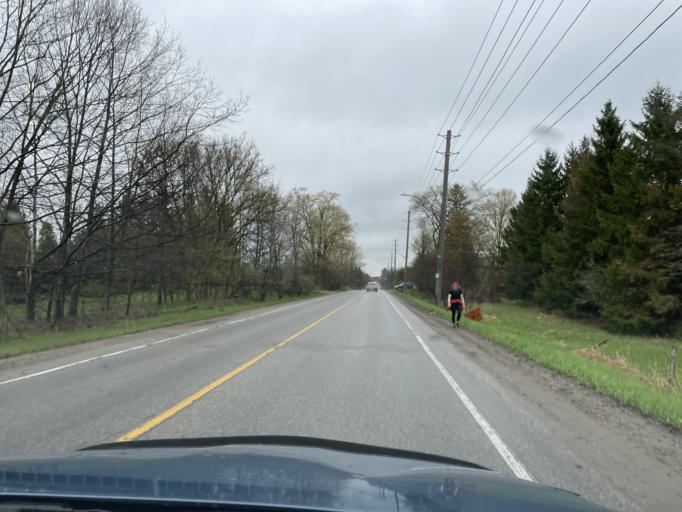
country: CA
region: Ontario
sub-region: Wellington County
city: Guelph
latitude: 43.5394
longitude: -80.2226
